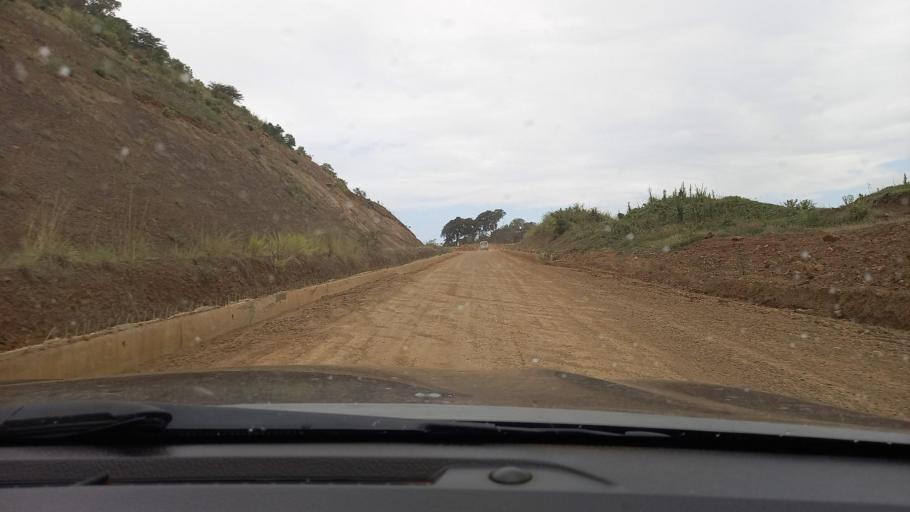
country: ET
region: Southern Nations, Nationalities, and People's Region
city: Mizan Teferi
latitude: 6.2018
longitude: 35.6747
